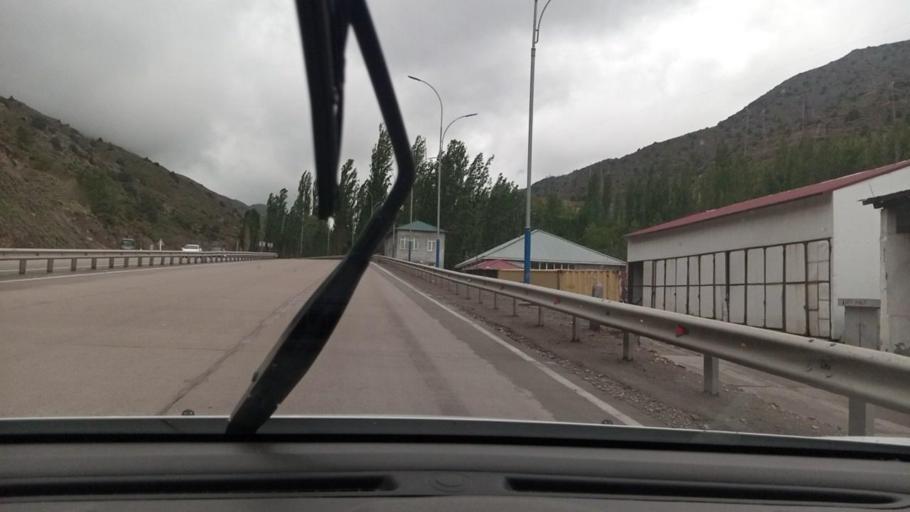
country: TJ
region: Viloyati Sughd
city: Shaydon
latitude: 41.0395
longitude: 70.5788
